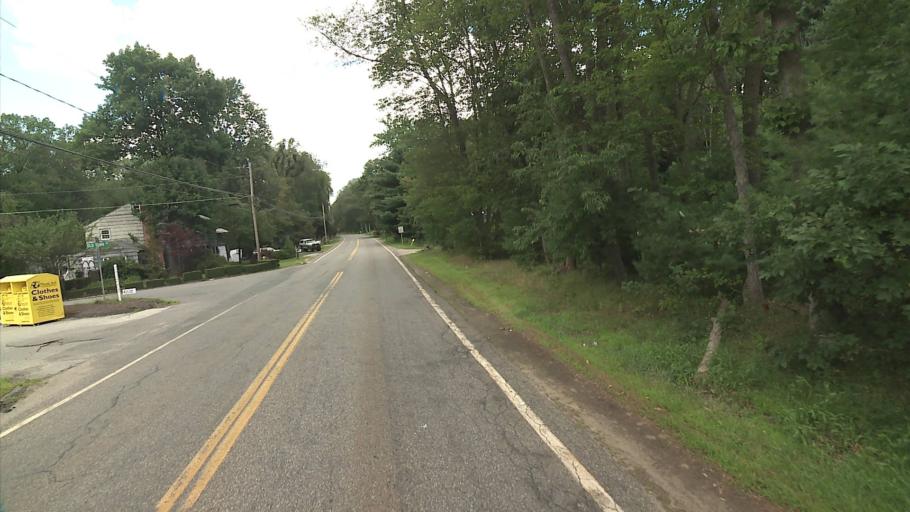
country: US
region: Connecticut
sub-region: Tolland County
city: Stafford
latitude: 41.9350
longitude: -72.1929
